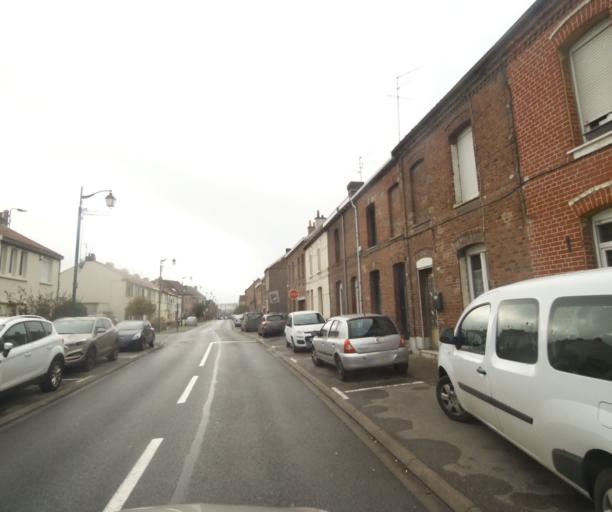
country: FR
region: Nord-Pas-de-Calais
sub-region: Departement du Nord
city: Aulnoy-lez-Valenciennes
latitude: 50.3362
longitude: 3.5274
